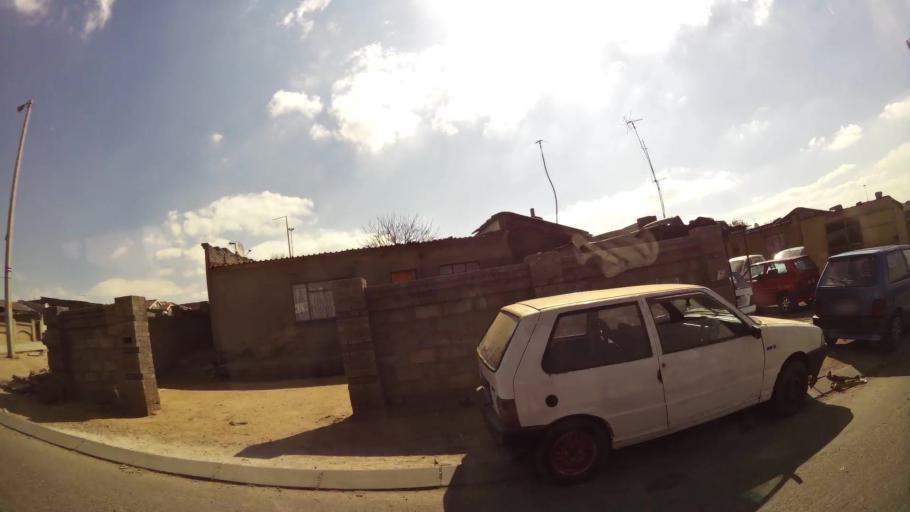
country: ZA
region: Gauteng
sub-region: Ekurhuleni Metropolitan Municipality
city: Tembisa
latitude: -26.0173
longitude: 28.1993
